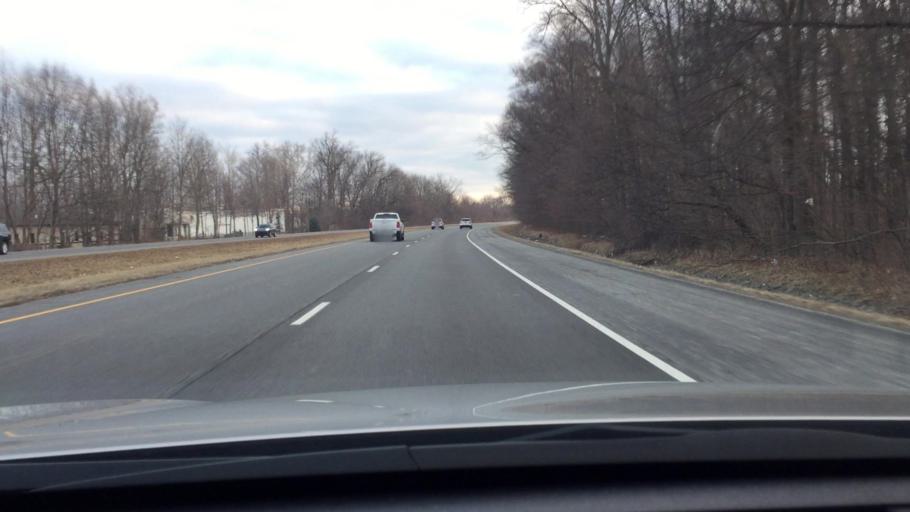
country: US
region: Indiana
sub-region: Hamilton County
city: Noblesville
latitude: 40.0132
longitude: -86.0030
